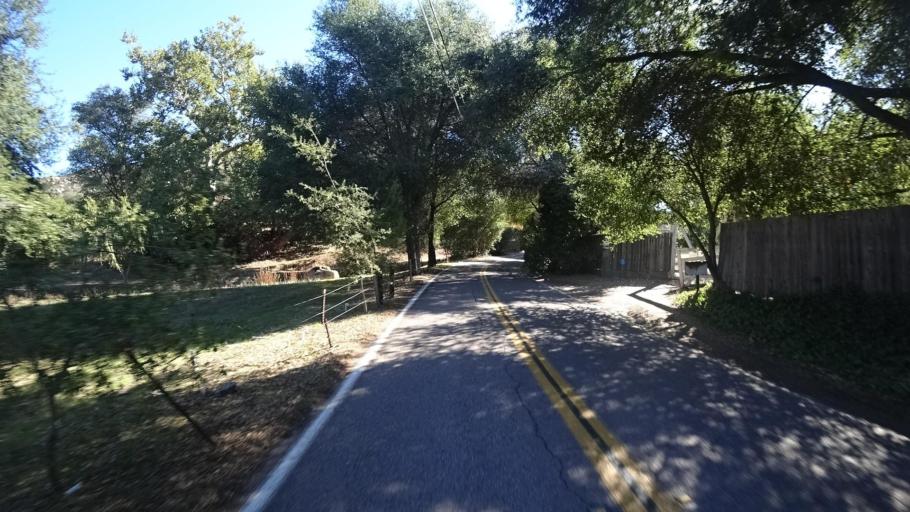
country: US
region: California
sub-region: San Diego County
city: Jamul
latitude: 32.7142
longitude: -116.7569
